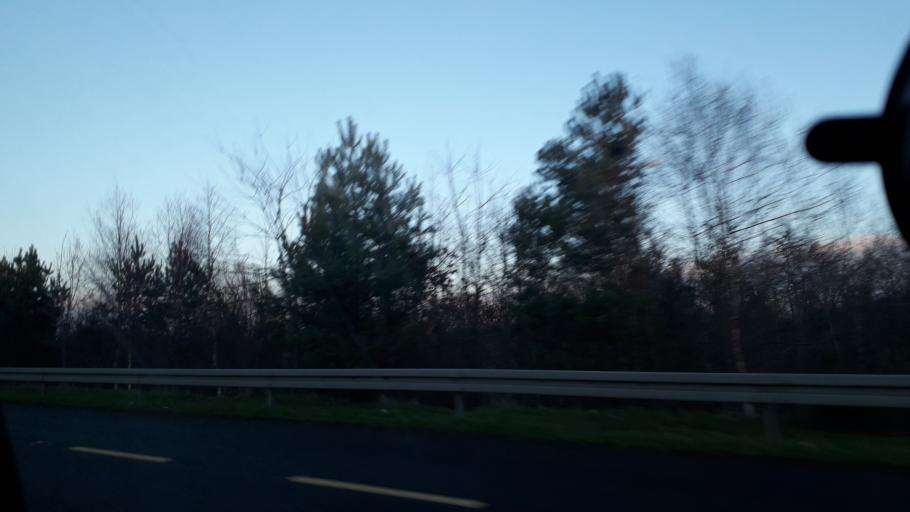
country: IE
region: Ulster
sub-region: County Monaghan
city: Monaghan
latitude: 54.2456
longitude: -6.9449
